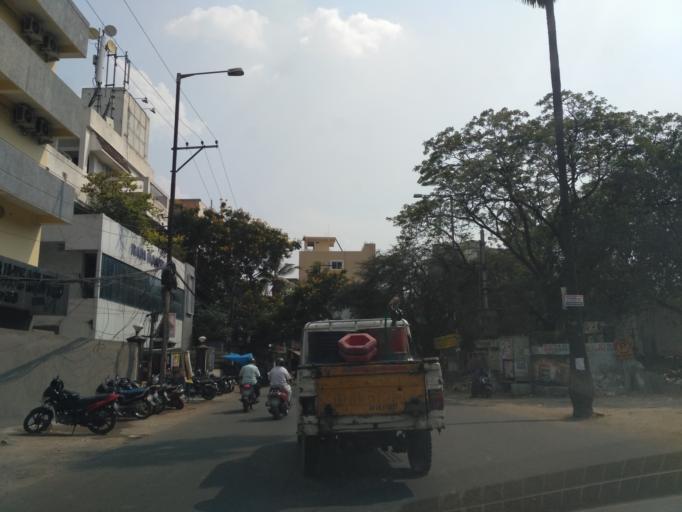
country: IN
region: Telangana
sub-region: Rangareddi
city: Kukatpalli
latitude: 17.4370
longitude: 78.4399
